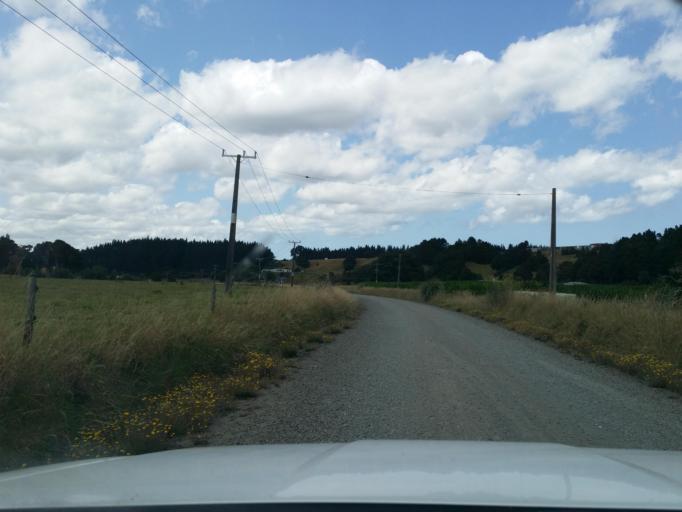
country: NZ
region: Northland
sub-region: Kaipara District
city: Dargaville
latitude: -35.8072
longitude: 173.7309
